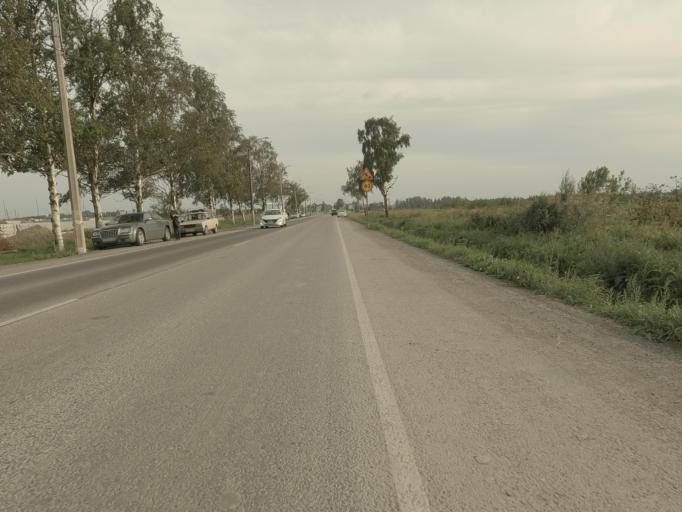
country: RU
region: St.-Petersburg
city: Strel'na
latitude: 59.8435
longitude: 30.0910
